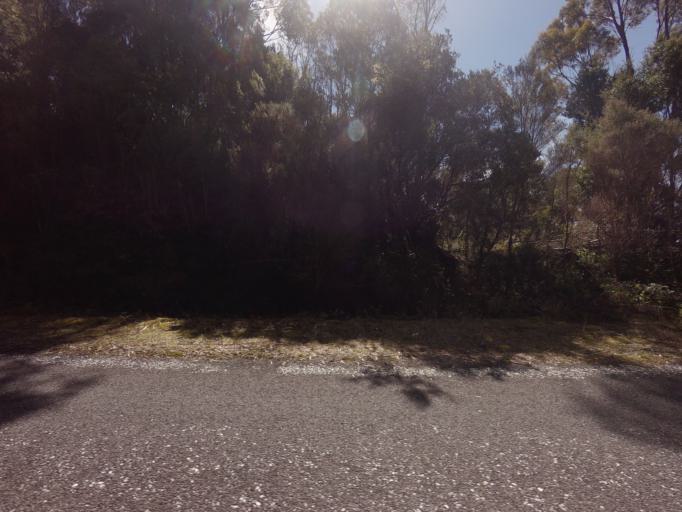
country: AU
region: Tasmania
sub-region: West Coast
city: Queenstown
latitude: -42.7518
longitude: 145.9971
